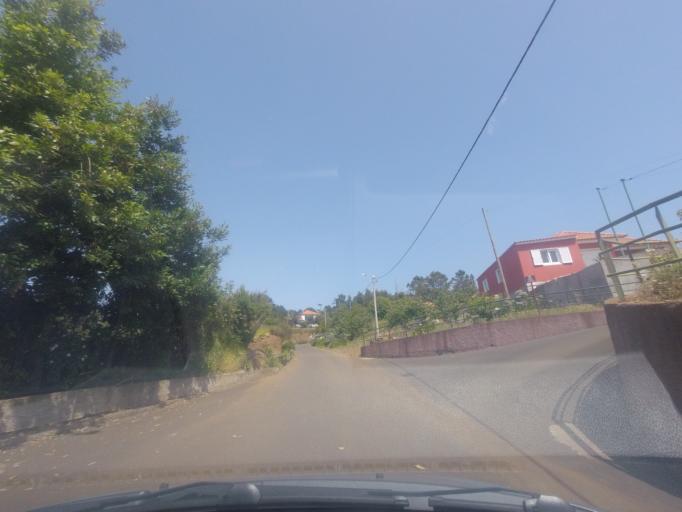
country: PT
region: Madeira
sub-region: Calheta
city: Faja da Ovelha
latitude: 32.8008
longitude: -17.2344
